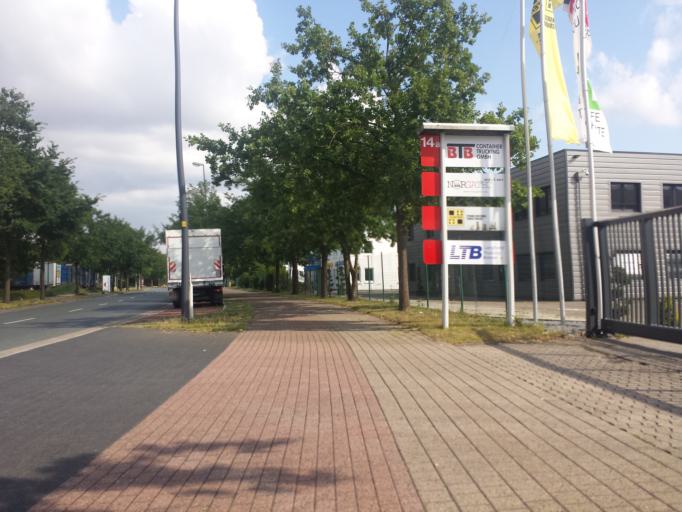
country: DE
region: Lower Saxony
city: Stuhr
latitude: 53.0870
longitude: 8.7131
